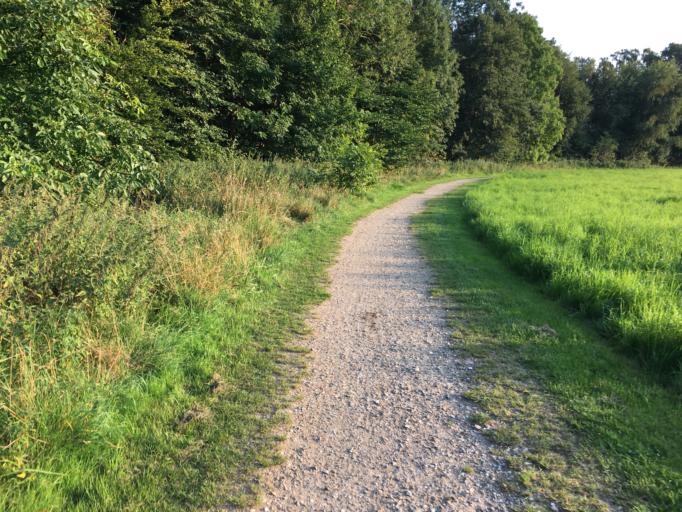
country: DK
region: Capital Region
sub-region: Fredensborg Kommune
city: Niva
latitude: 55.9287
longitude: 12.5078
